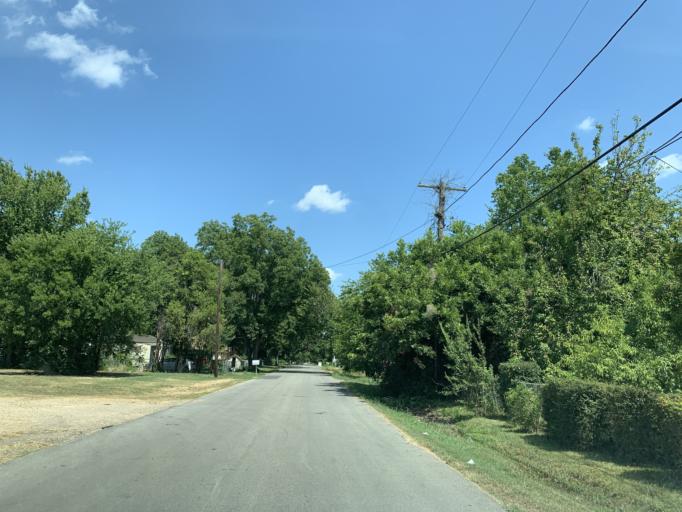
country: US
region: Texas
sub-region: Dallas County
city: Hutchins
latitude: 32.7064
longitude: -96.7651
